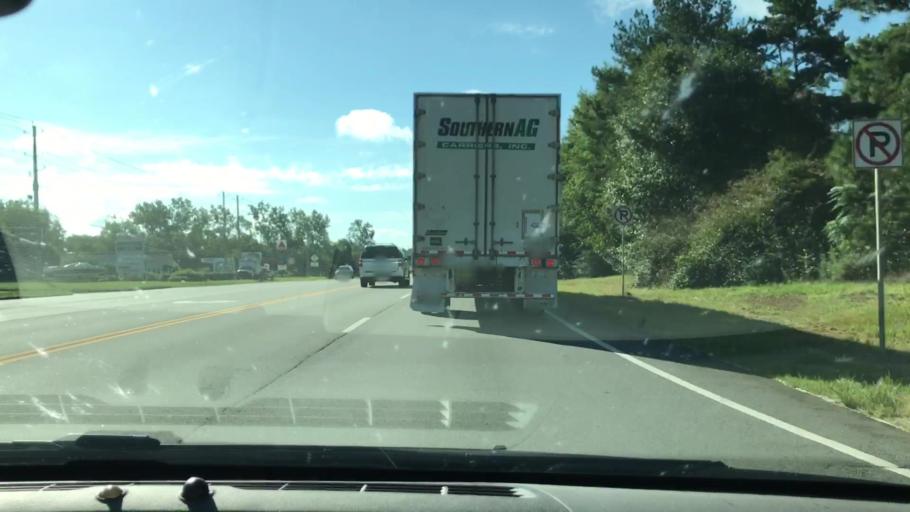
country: US
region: Georgia
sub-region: Dougherty County
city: Albany
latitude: 31.6355
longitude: -84.2462
